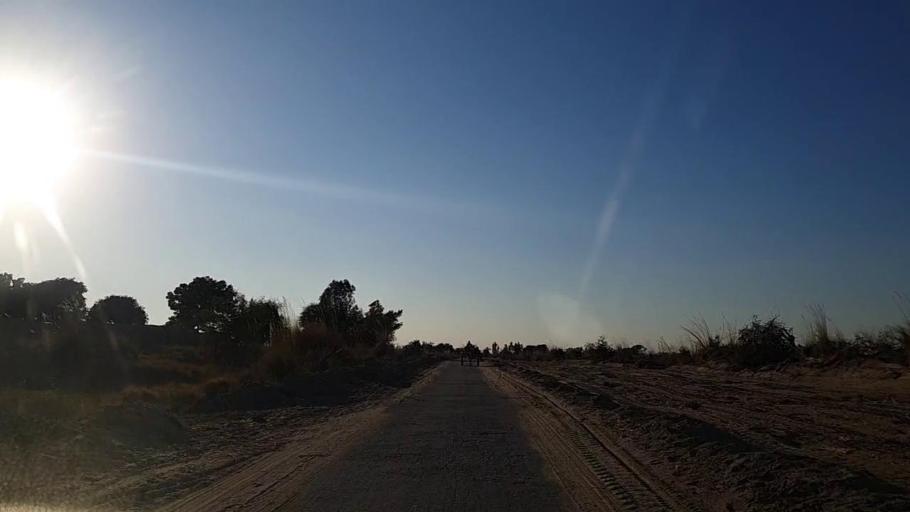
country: PK
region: Sindh
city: Khadro
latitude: 26.2791
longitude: 68.8657
